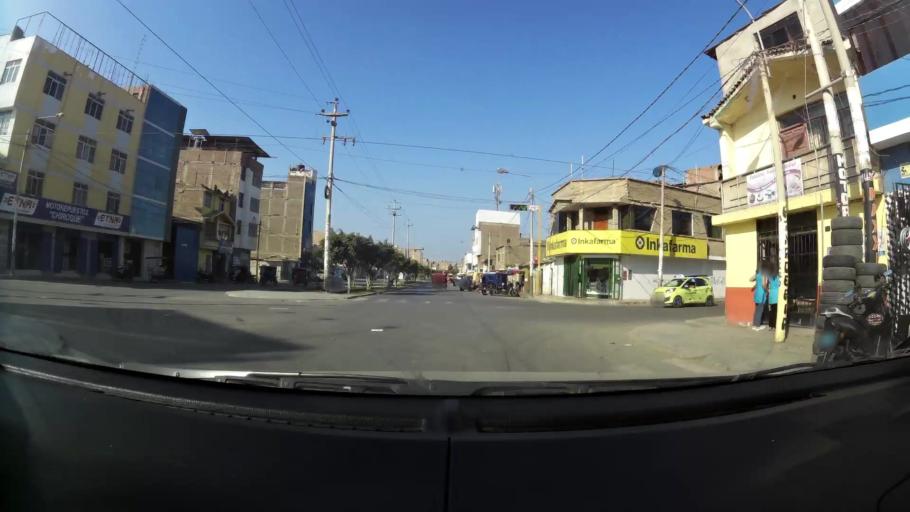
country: PE
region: Lambayeque
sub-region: Provincia de Chiclayo
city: Chiclayo
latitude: -6.7644
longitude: -79.8510
